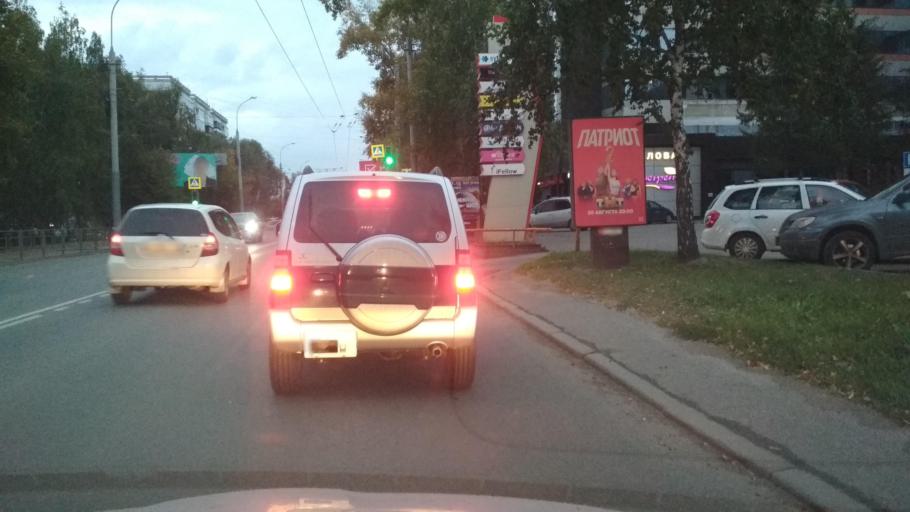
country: RU
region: Tomsk
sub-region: Tomskiy Rayon
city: Tomsk
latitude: 56.4761
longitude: 84.9856
